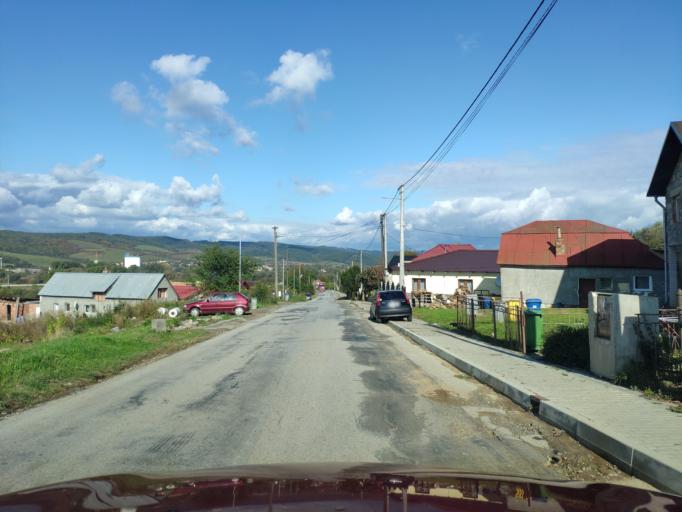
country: SK
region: Presovsky
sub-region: Okres Presov
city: Presov
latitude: 48.9082
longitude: 21.2614
